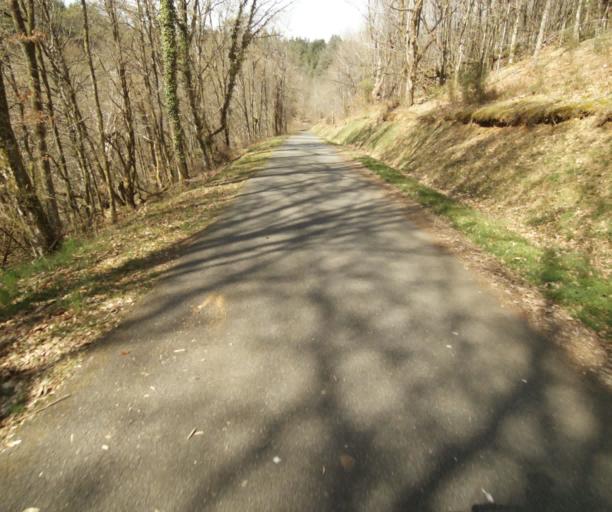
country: FR
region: Limousin
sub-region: Departement de la Correze
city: Seilhac
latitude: 45.4016
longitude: 1.7808
